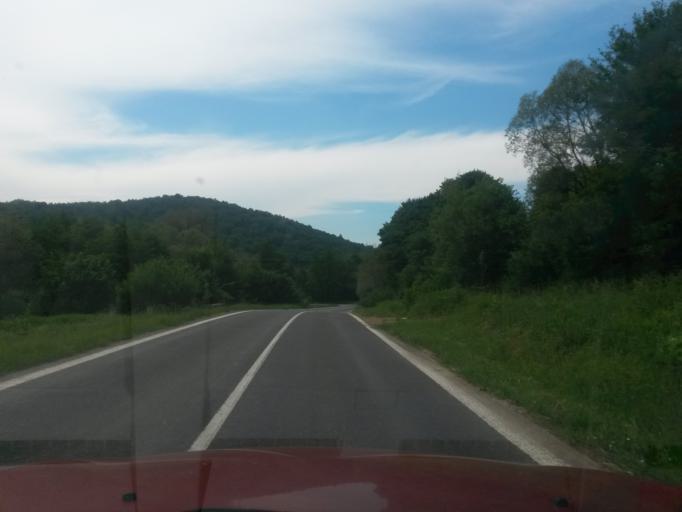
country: SK
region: Presovsky
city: Snina
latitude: 48.9892
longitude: 22.2440
